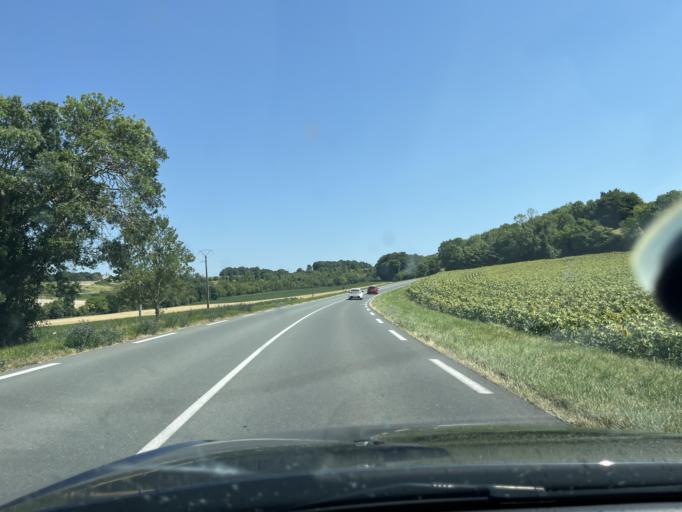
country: FR
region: Poitou-Charentes
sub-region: Departement de la Charente-Maritime
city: Mirambeau
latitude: 45.4111
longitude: -0.6098
